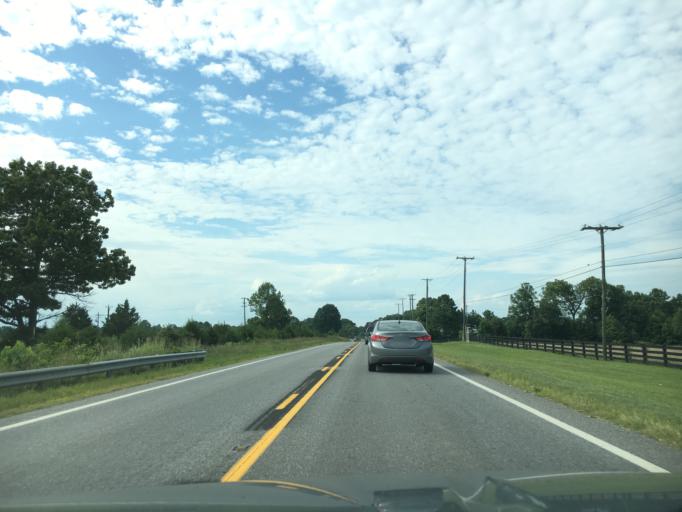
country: US
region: Virginia
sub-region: Campbell County
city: Brookneal
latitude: 37.0792
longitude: -78.9855
